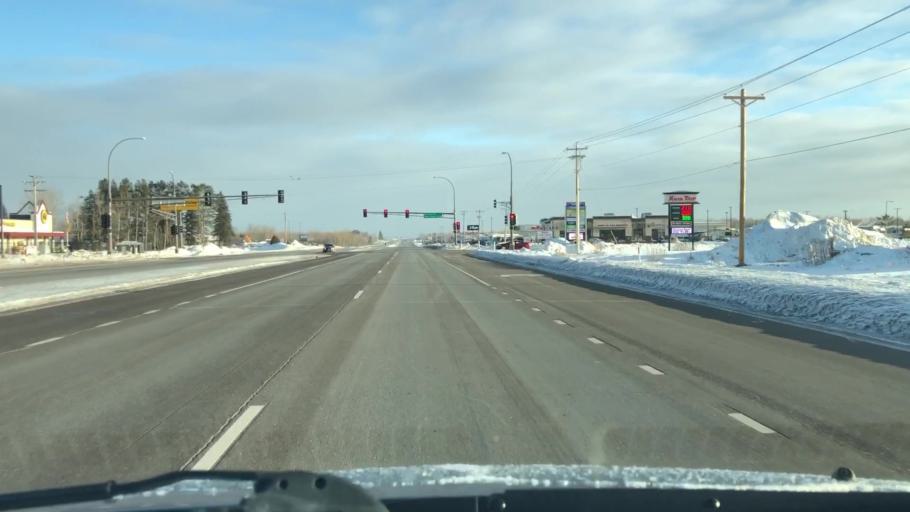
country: US
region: Minnesota
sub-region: Saint Louis County
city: Hermantown
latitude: 46.8342
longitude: -92.2065
